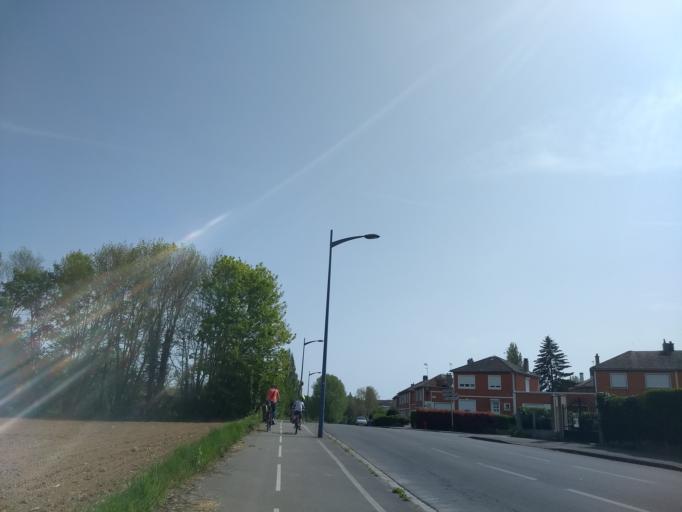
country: FR
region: Nord-Pas-de-Calais
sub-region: Departement du Pas-de-Calais
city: Anzin-Saint-Aubin
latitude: 50.3050
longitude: 2.7475
